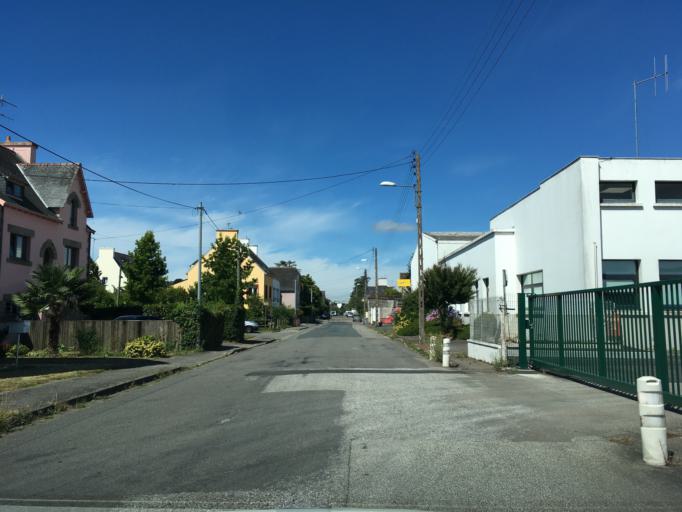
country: FR
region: Brittany
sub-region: Departement du Finistere
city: Quimper
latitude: 47.9951
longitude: -4.0786
